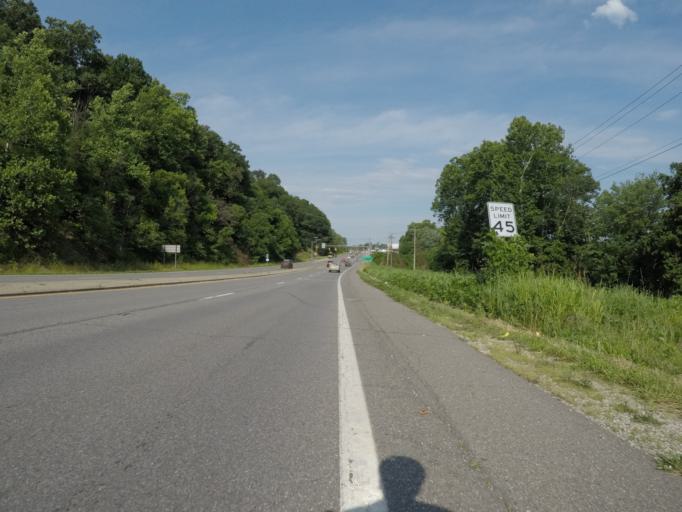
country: US
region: West Virginia
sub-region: Cabell County
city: Pea Ridge
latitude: 38.4120
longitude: -82.3183
